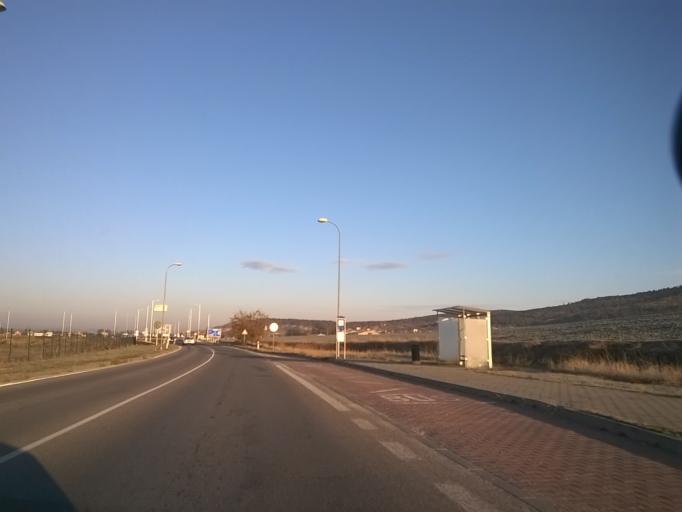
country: SK
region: Nitriansky
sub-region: Okres Nitra
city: Nitra
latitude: 48.3415
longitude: 18.0667
